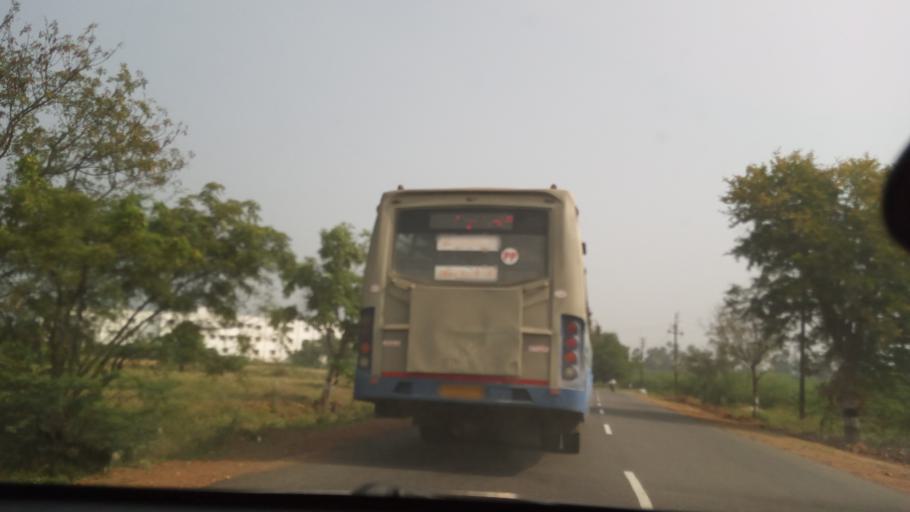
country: IN
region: Tamil Nadu
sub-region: Erode
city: Punjai Puliyampatti
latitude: 11.4226
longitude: 77.1940
